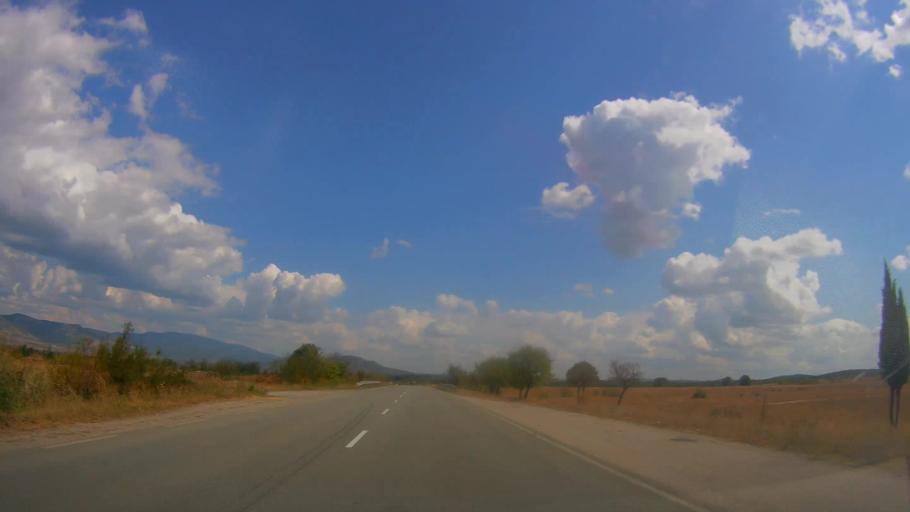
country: BG
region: Sliven
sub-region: Obshtina Tvurditsa
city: Tvurditsa
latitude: 42.6545
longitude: 25.9427
